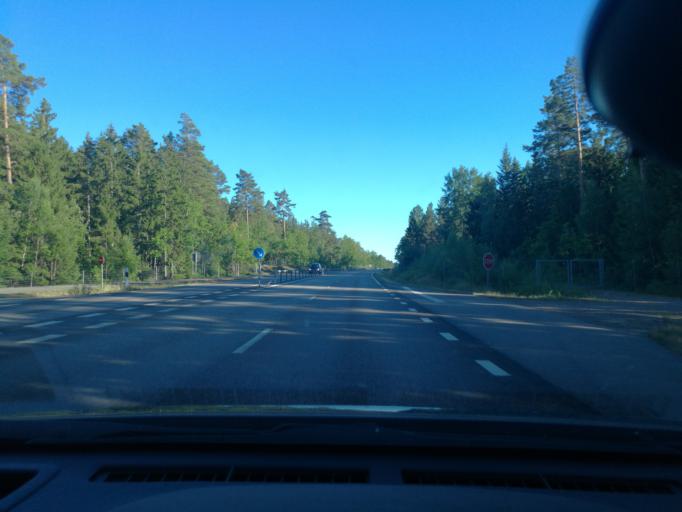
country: SE
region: Kalmar
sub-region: Monsteras Kommun
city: Timmernabben
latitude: 56.8853
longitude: 16.3825
